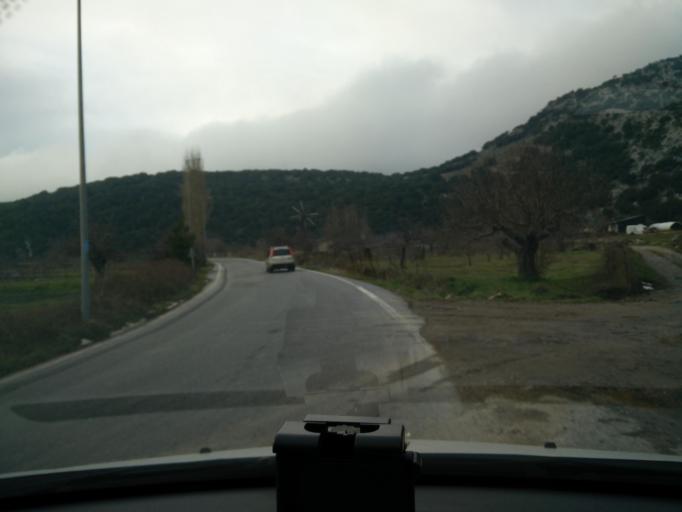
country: GR
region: Crete
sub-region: Nomos Irakleiou
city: Malia
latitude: 35.2032
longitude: 25.4789
